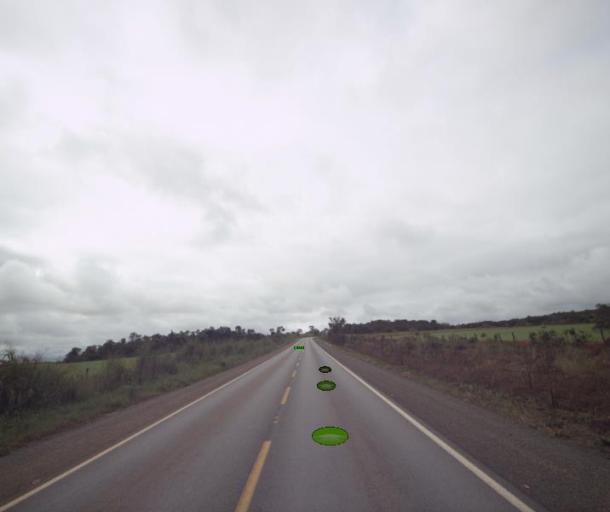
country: BR
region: Goias
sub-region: Uruacu
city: Uruacu
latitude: -14.6726
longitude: -49.1406
